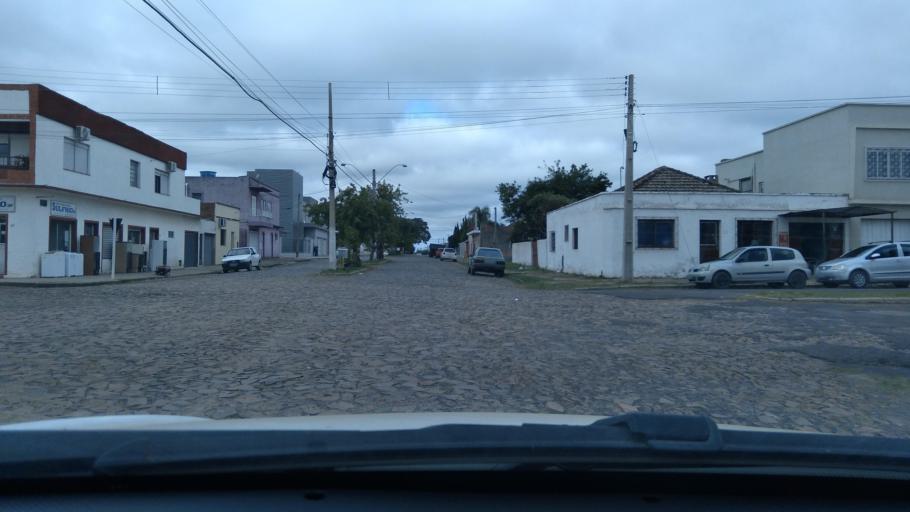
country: BR
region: Rio Grande do Sul
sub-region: Dom Pedrito
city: Dom Pedrito
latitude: -30.9810
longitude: -54.6693
